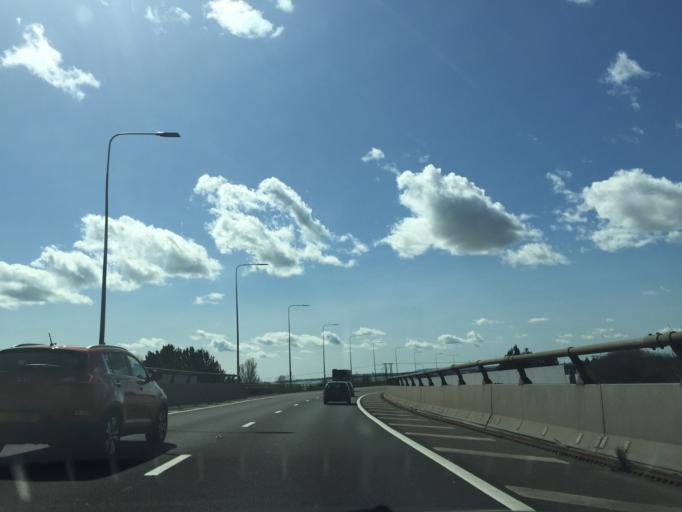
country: GB
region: England
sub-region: Hampshire
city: Havant
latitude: 50.8472
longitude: -1.0120
